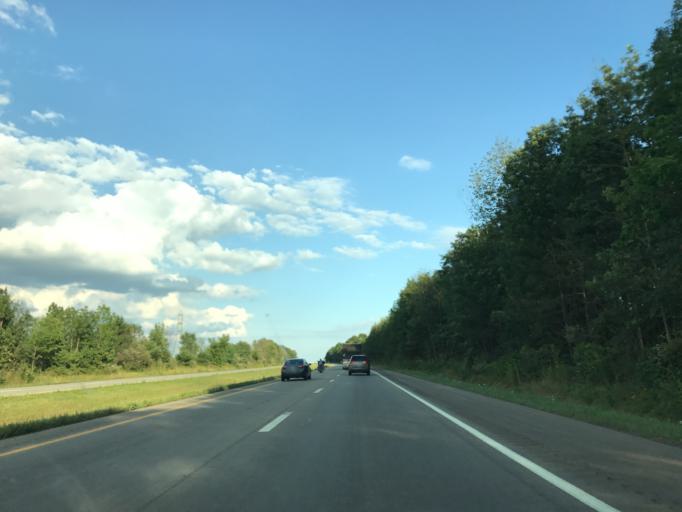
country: US
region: Ohio
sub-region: Wayne County
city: Dalton
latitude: 40.7952
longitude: -81.6450
